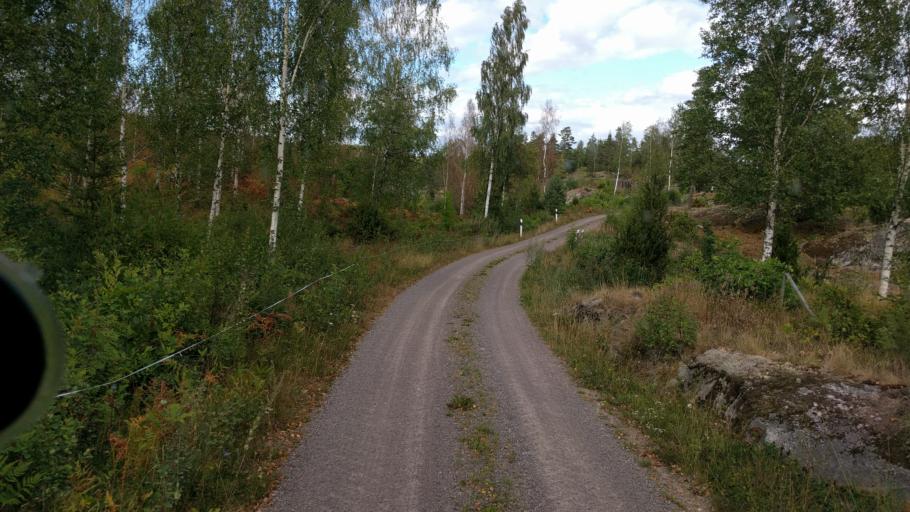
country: SE
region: Kalmar
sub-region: Vasterviks Kommun
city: Ankarsrum
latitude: 57.7236
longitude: 16.0905
